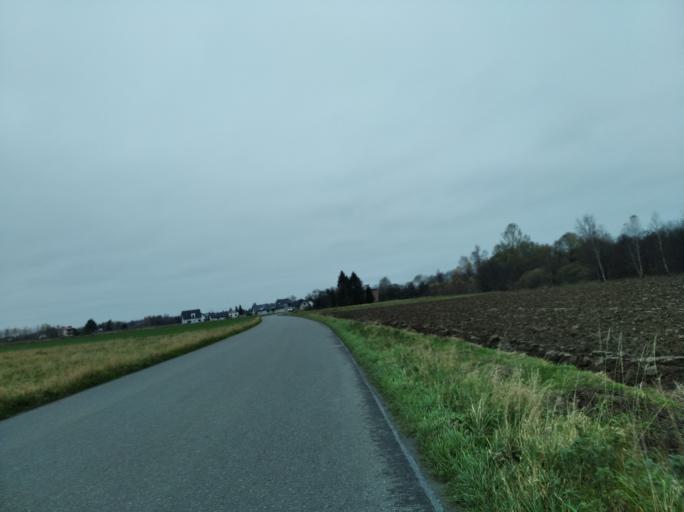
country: PL
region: Subcarpathian Voivodeship
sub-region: Powiat krosnienski
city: Chorkowka
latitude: 49.6784
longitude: 21.6790
